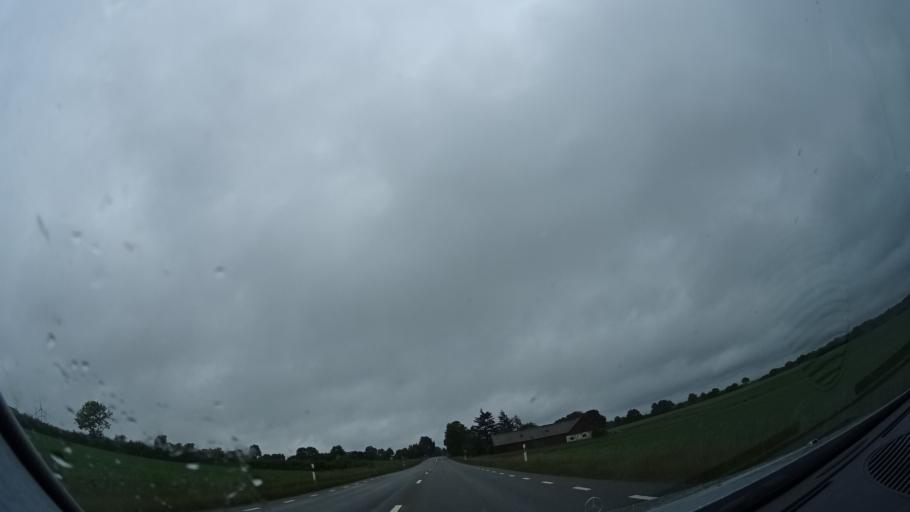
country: SE
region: Skane
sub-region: Hoors Kommun
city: Loberod
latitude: 55.8308
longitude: 13.4915
